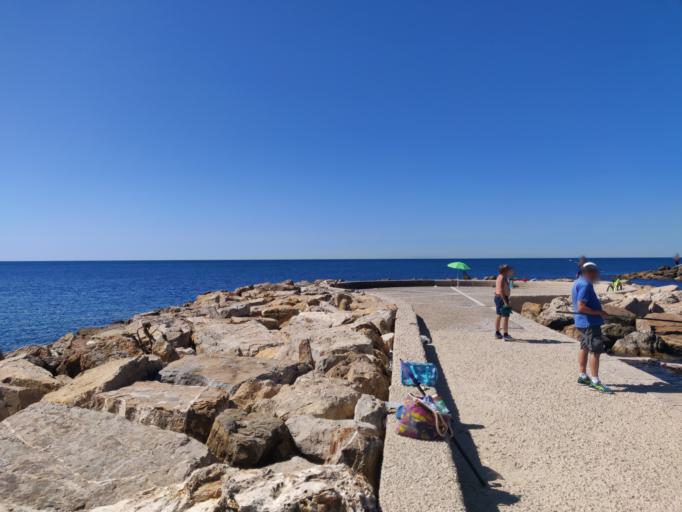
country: IT
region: Latium
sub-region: Citta metropolitana di Roma Capitale
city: Civitavecchia
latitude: 42.0884
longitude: 11.7923
